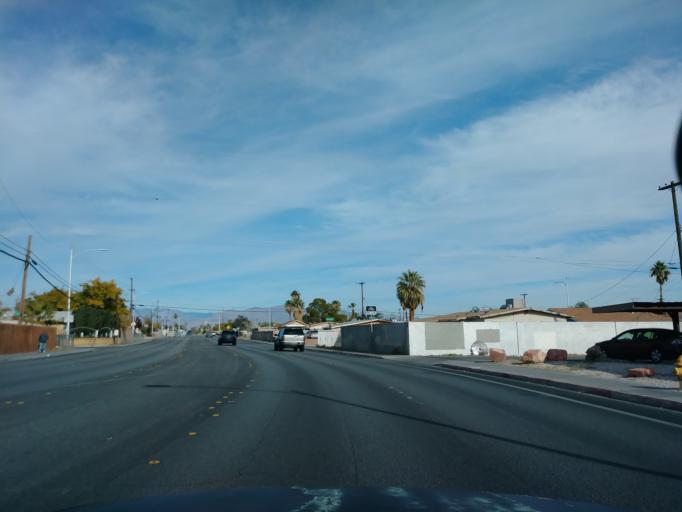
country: US
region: Nevada
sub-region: Clark County
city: Spring Valley
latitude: 36.1609
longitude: -115.2332
